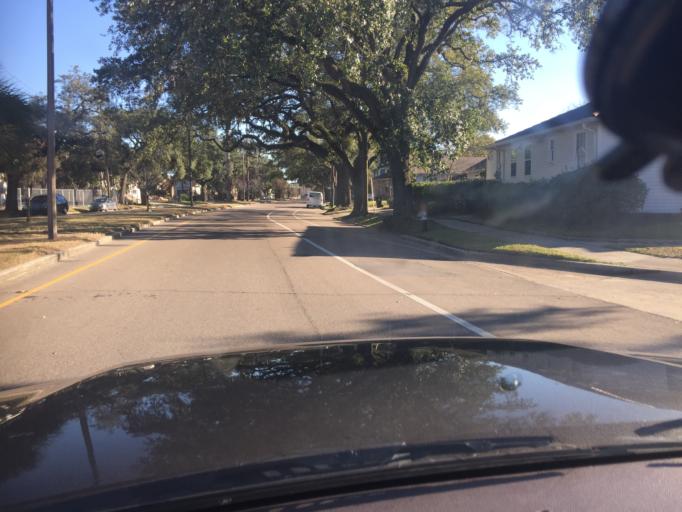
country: US
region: Louisiana
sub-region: Orleans Parish
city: New Orleans
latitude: 29.9880
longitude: -90.0746
